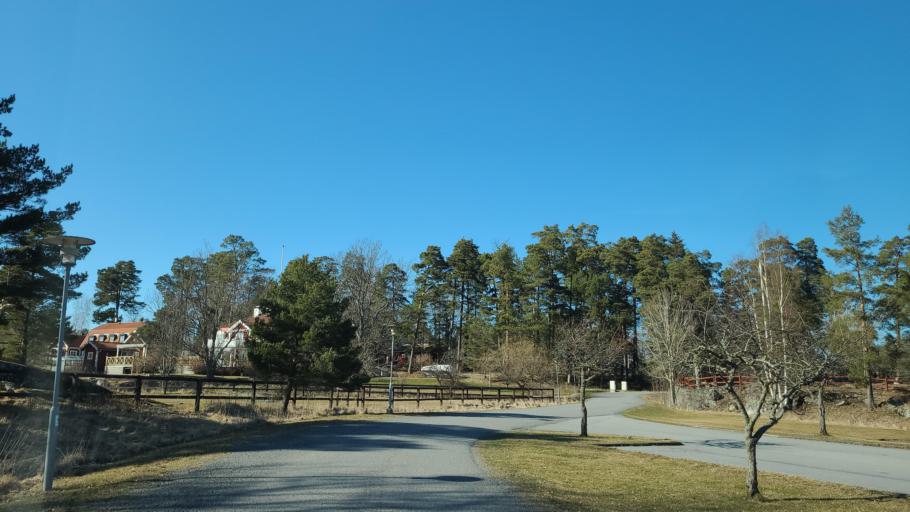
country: SE
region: Stockholm
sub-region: Varmdo Kommun
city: Hemmesta
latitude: 59.2768
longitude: 18.5615
